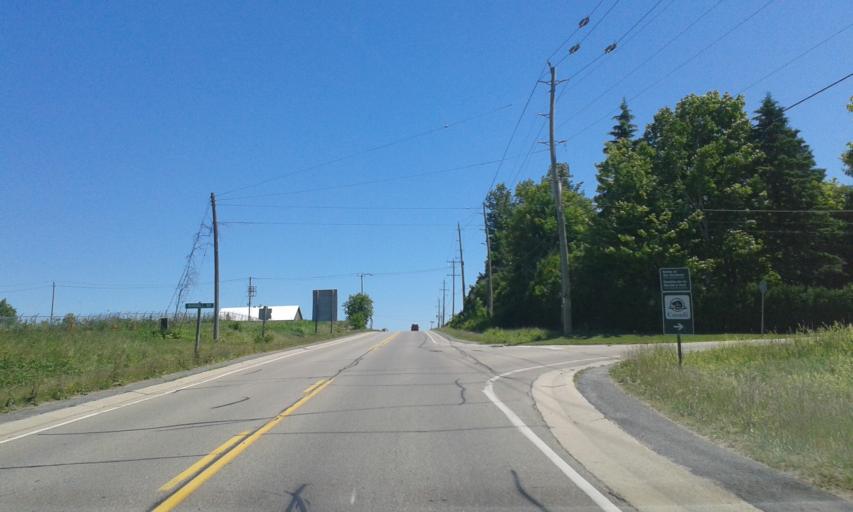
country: CA
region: Ontario
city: Prescott
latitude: 44.7216
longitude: -75.4916
